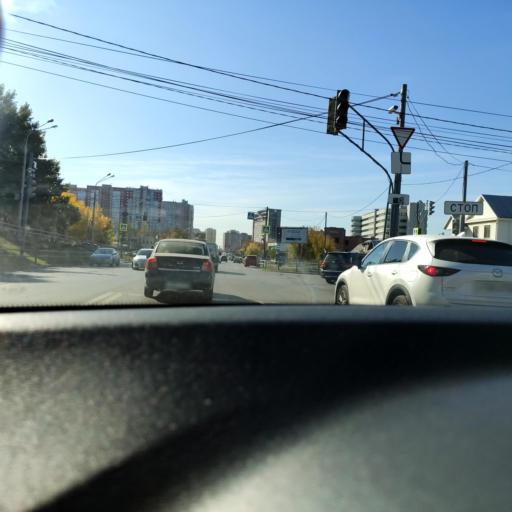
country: RU
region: Samara
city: Samara
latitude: 53.2647
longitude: 50.2117
